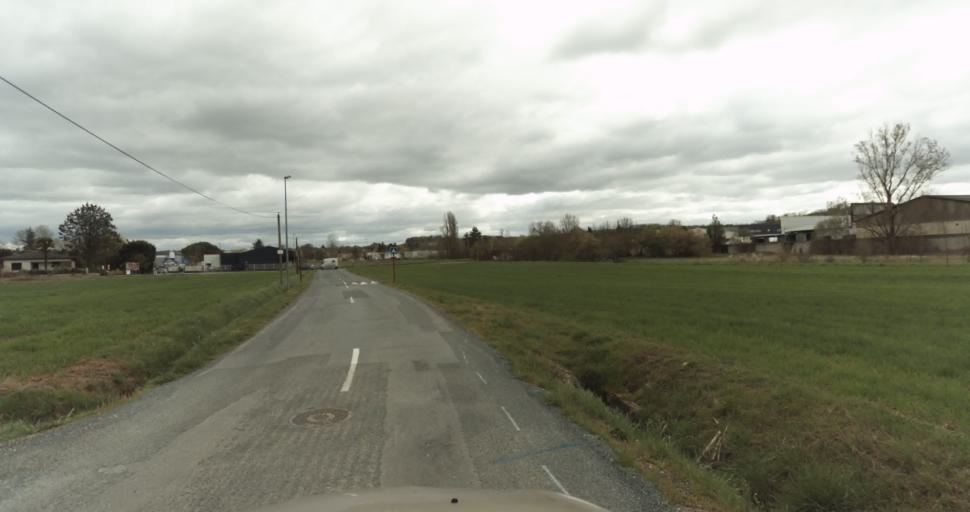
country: FR
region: Midi-Pyrenees
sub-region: Departement du Tarn
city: Puygouzon
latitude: 43.8965
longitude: 2.1549
